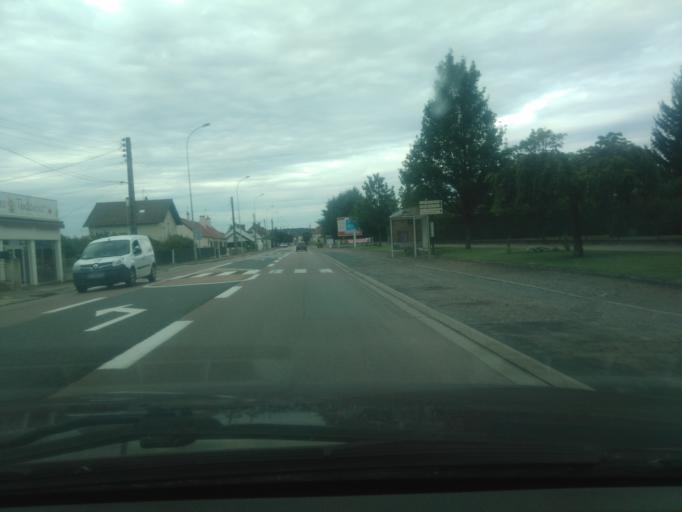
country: FR
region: Bourgogne
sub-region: Departement de la Nievre
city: Decize
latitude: 46.8227
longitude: 3.4522
